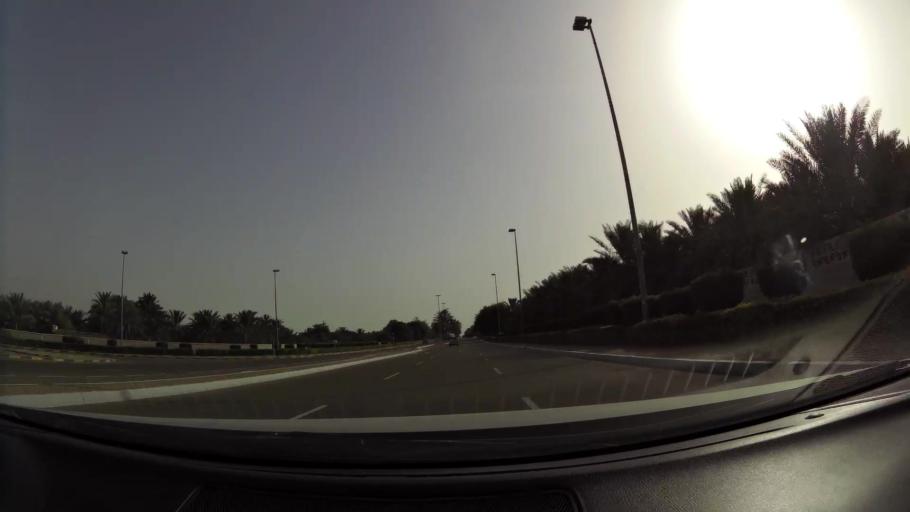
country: AE
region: Abu Dhabi
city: Al Ain
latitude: 24.1330
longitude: 55.6834
